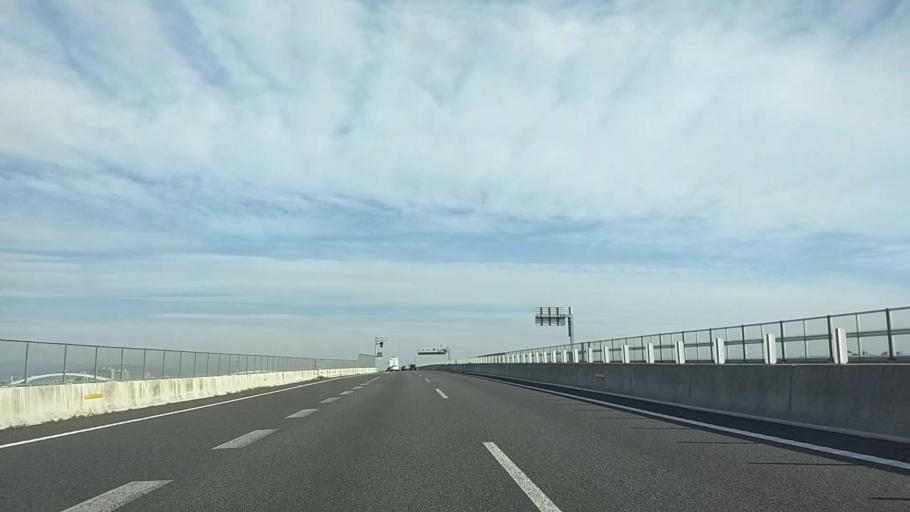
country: JP
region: Kanagawa
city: Atsugi
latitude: 35.4410
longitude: 139.3760
